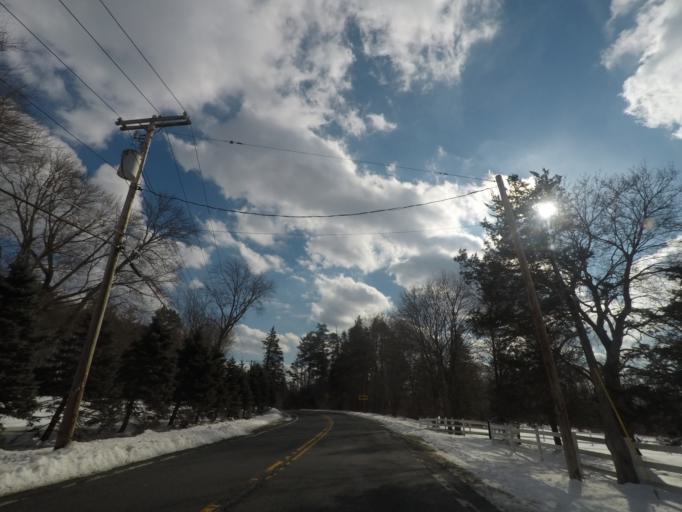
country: US
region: New York
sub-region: Schenectady County
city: Niskayuna
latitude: 42.8369
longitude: -73.8725
